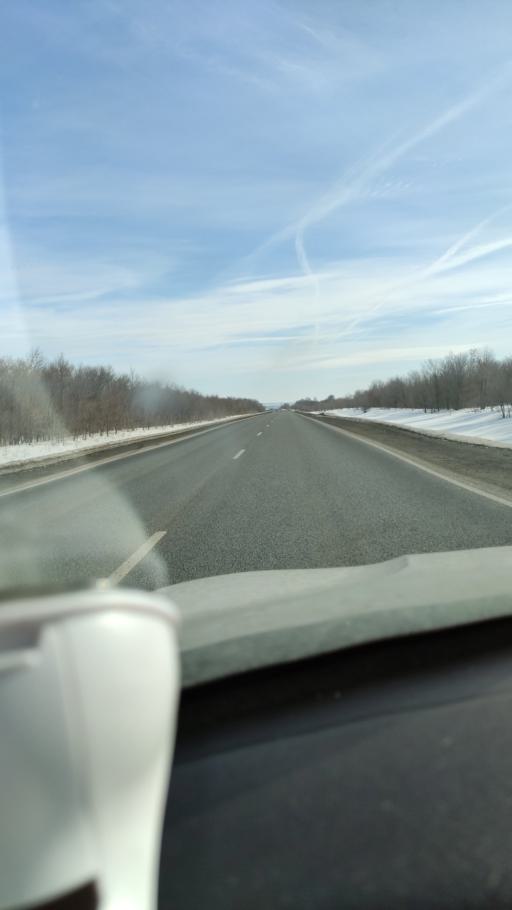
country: RU
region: Samara
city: Novokuybyshevsk
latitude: 52.9368
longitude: 49.9053
